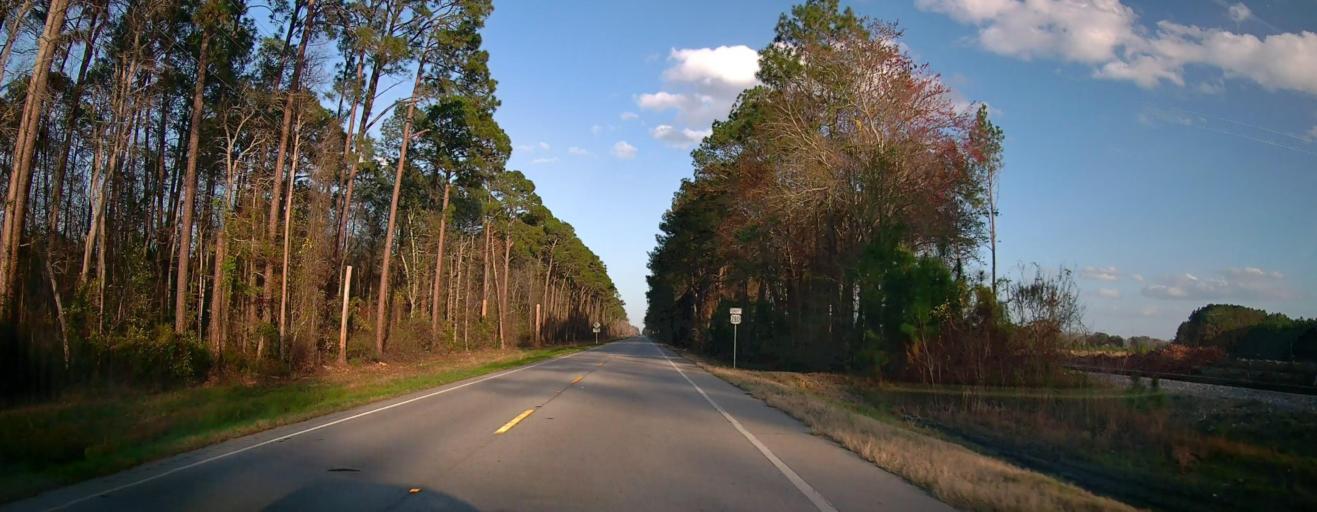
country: US
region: Georgia
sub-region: Bryan County
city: Pembroke
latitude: 32.1411
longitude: -81.6996
